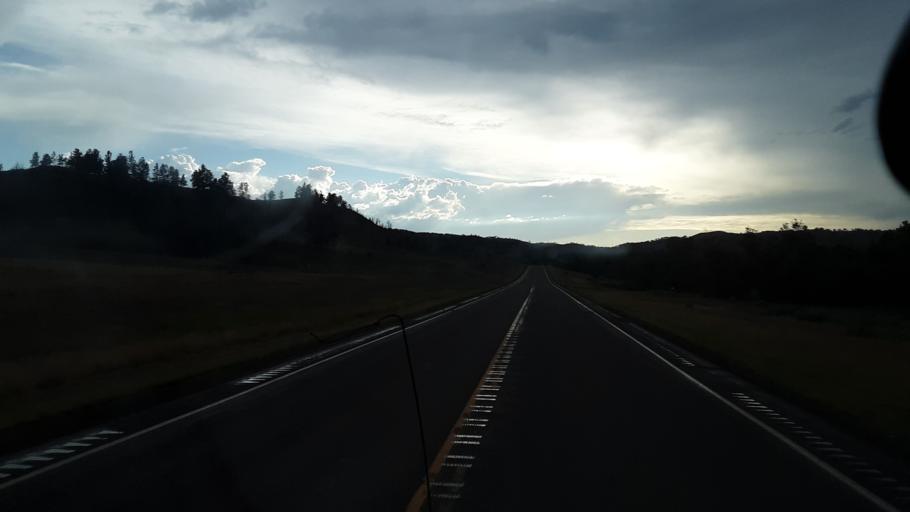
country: US
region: Montana
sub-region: Rosebud County
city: Lame Deer
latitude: 45.6183
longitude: -106.3966
